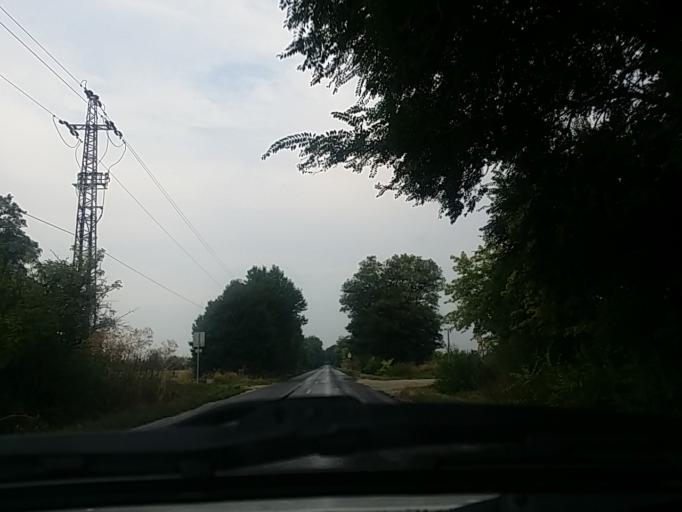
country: HU
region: Pest
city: Paty
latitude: 47.5163
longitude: 18.8064
